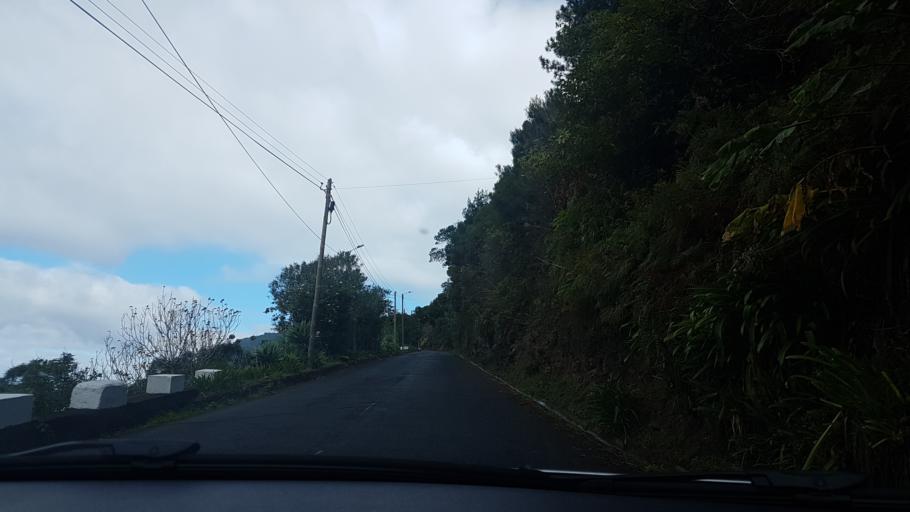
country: PT
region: Madeira
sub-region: Sao Vicente
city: Sao Vicente
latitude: 32.7783
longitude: -17.0306
